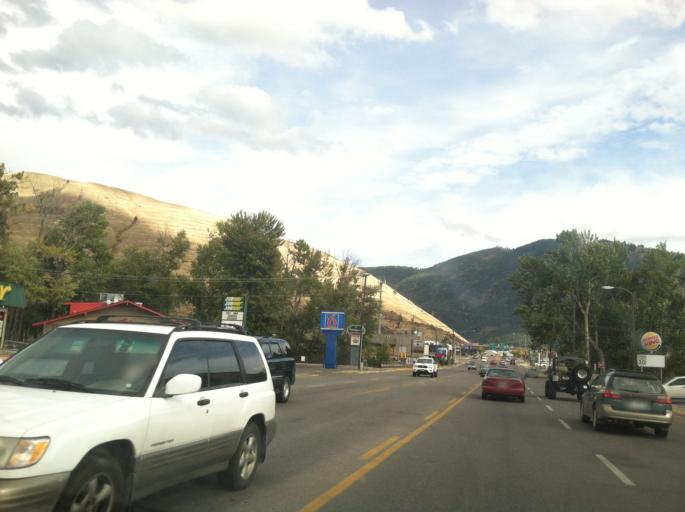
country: US
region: Montana
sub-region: Missoula County
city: Missoula
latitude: 46.8698
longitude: -113.9865
